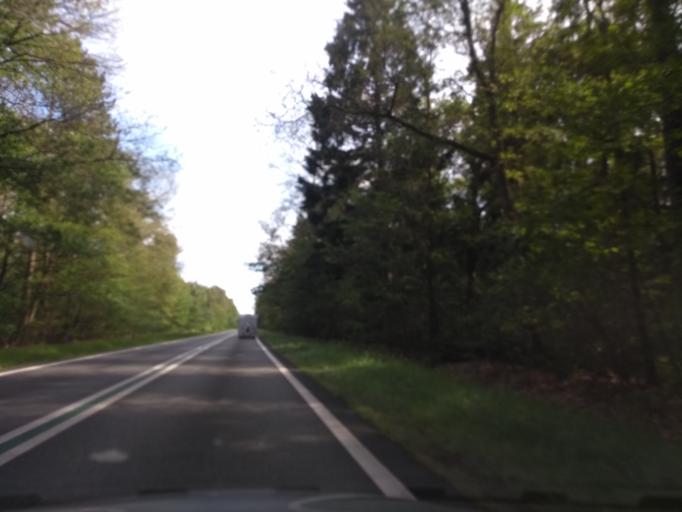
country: NL
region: Overijssel
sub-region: Gemeente Twenterand
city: Magele
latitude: 52.5429
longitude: 6.5443
